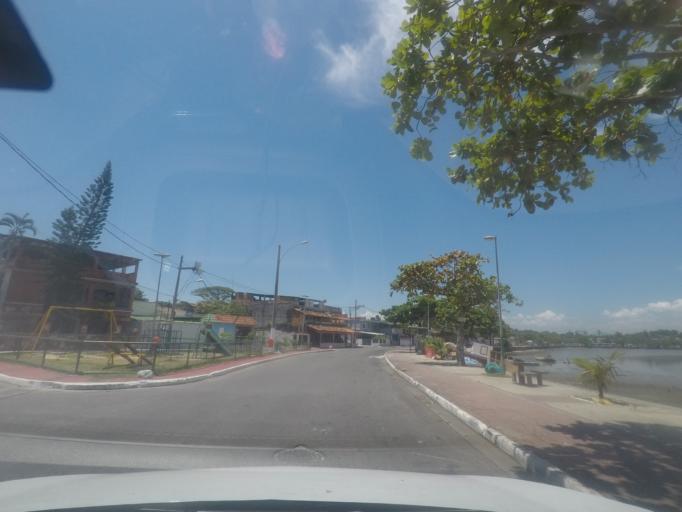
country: BR
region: Rio de Janeiro
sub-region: Itaguai
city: Itaguai
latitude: -22.9888
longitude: -43.6891
